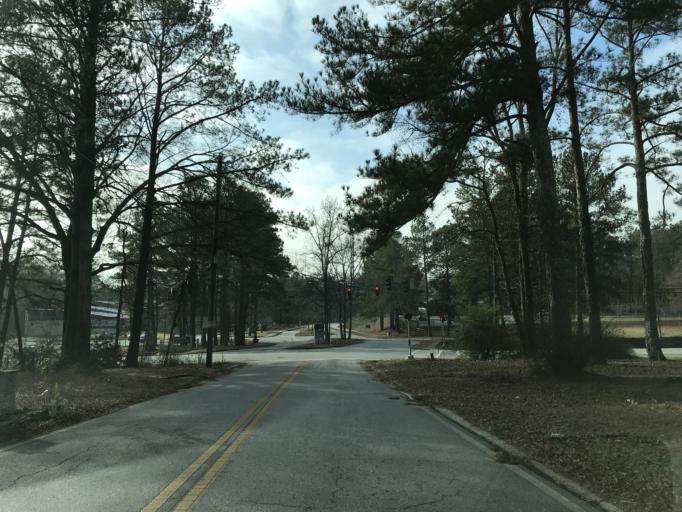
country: US
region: Georgia
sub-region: Clayton County
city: Jonesboro
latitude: 33.5552
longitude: -84.3634
